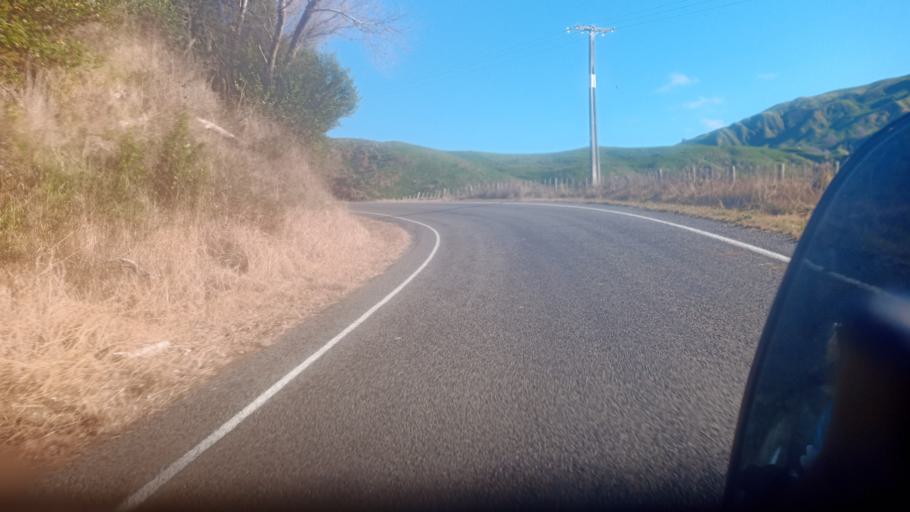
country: NZ
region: Gisborne
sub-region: Gisborne District
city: Gisborne
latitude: -38.5736
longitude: 177.5840
